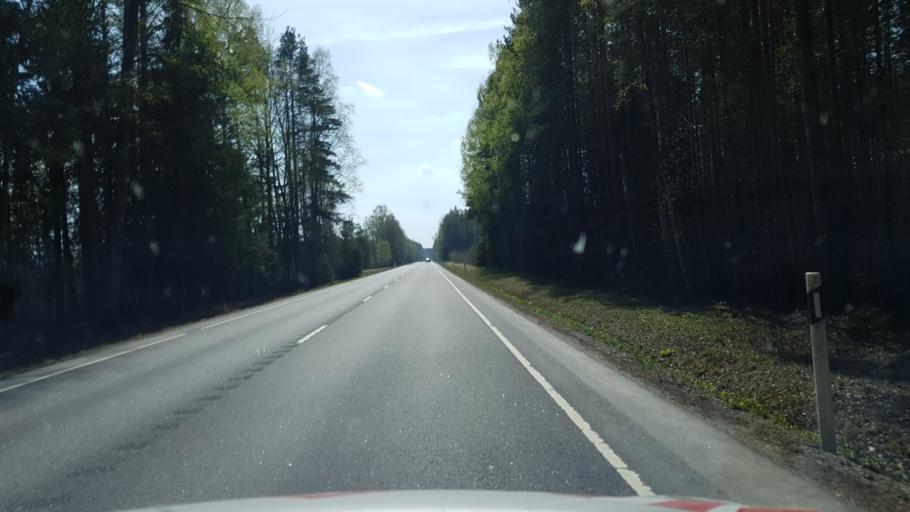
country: EE
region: Jaervamaa
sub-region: Tueri vald
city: Sarevere
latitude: 58.7123
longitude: 25.2699
